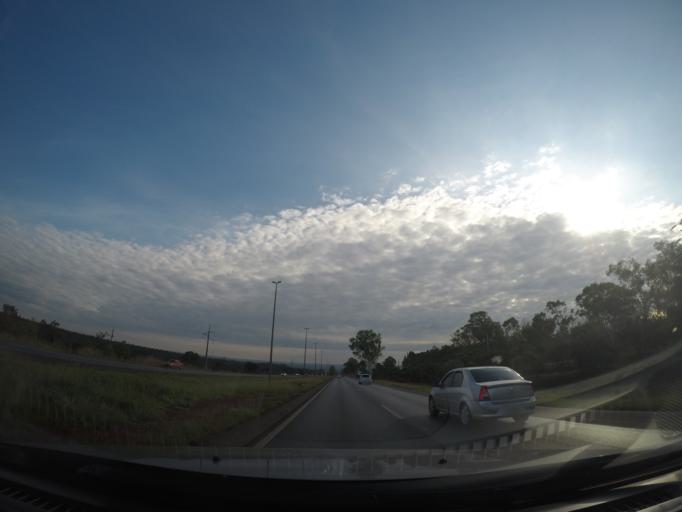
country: BR
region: Goias
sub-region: Planaltina
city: Planaltina
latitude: -15.6274
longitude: -47.7278
